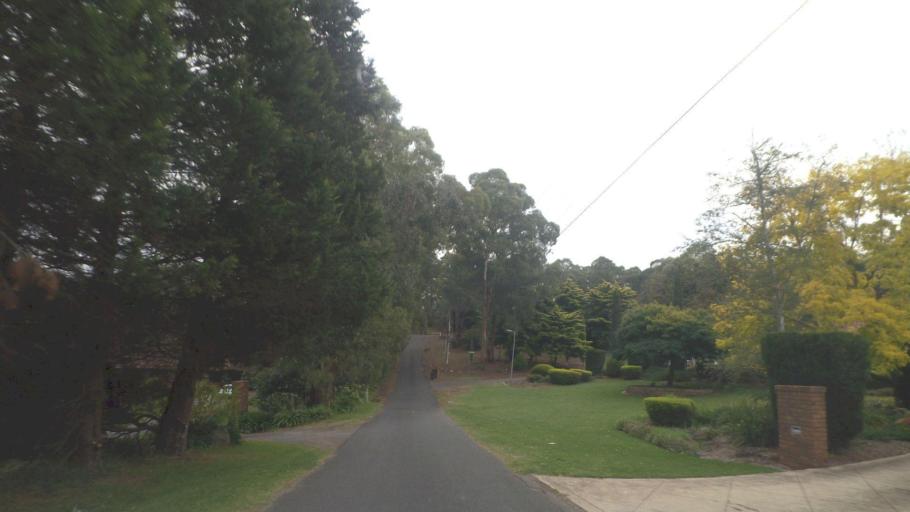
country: AU
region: Victoria
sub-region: Manningham
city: Park Orchards
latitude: -37.7605
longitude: 145.1900
